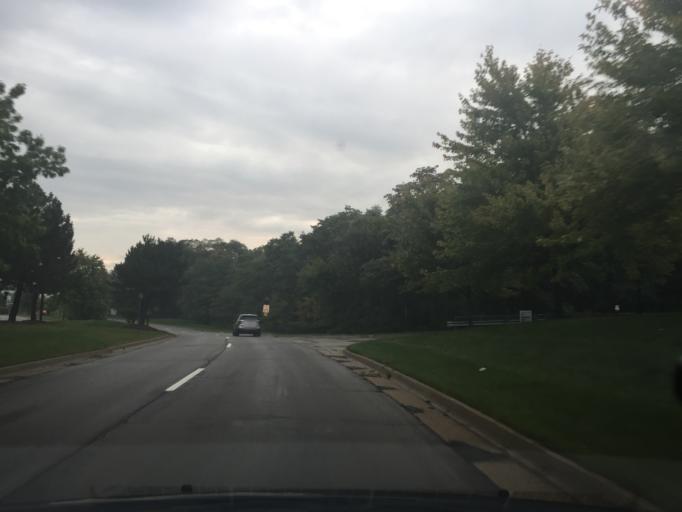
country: US
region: Michigan
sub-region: Oakland County
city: Auburn Hills
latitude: 42.6444
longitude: -83.2447
